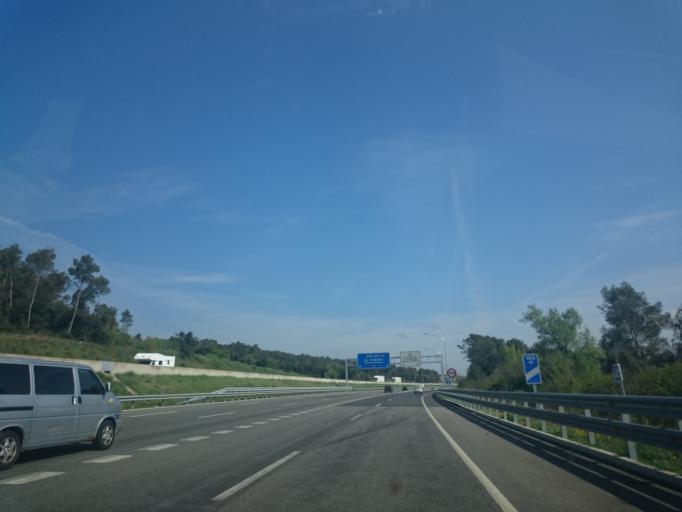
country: ES
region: Catalonia
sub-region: Provincia de Girona
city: Cervia de Ter
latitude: 42.0697
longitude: 2.8870
